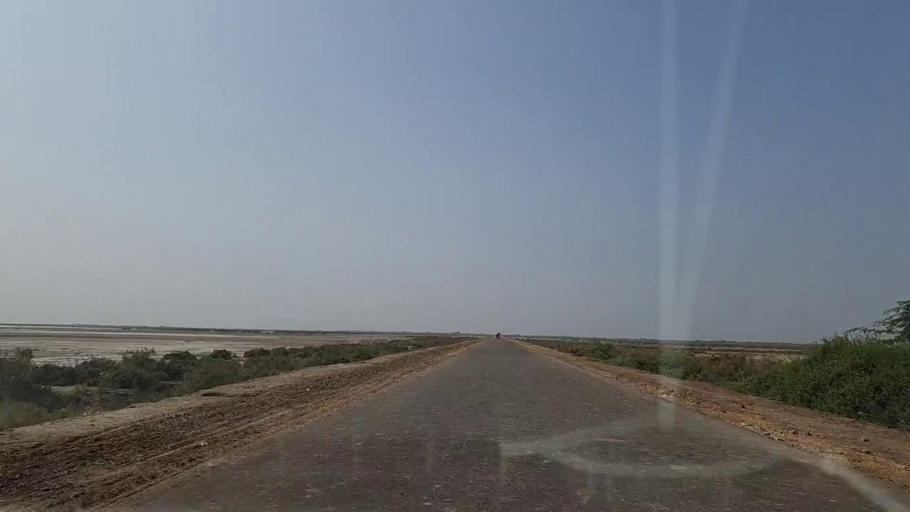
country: PK
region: Sindh
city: Chuhar Jamali
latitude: 24.2223
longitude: 67.8939
